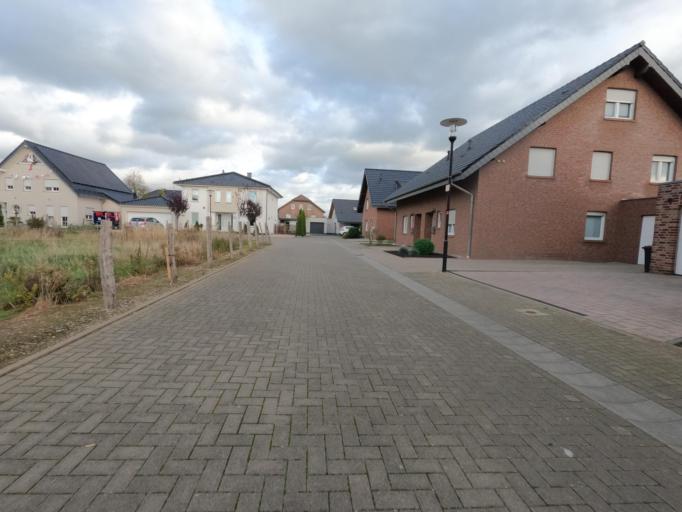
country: DE
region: North Rhine-Westphalia
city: Geilenkirchen
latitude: 50.9736
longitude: 6.1109
